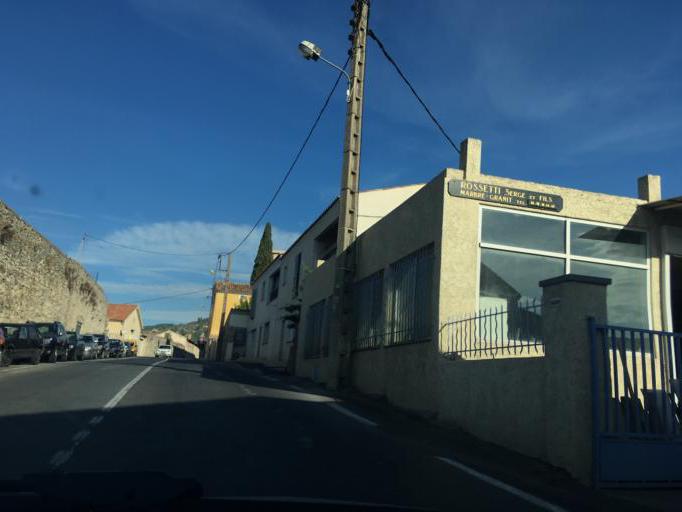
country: FR
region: Provence-Alpes-Cote d'Azur
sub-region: Departement du Var
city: Draguignan
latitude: 43.5373
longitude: 6.4699
